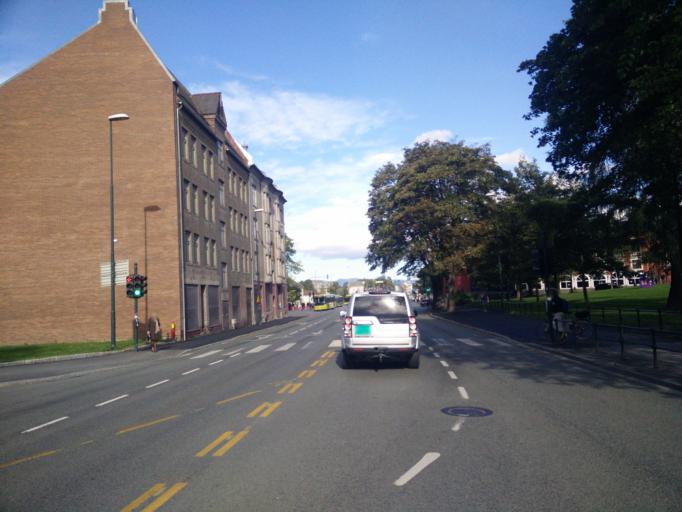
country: NO
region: Sor-Trondelag
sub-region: Trondheim
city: Trondheim
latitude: 63.4212
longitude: 10.3952
